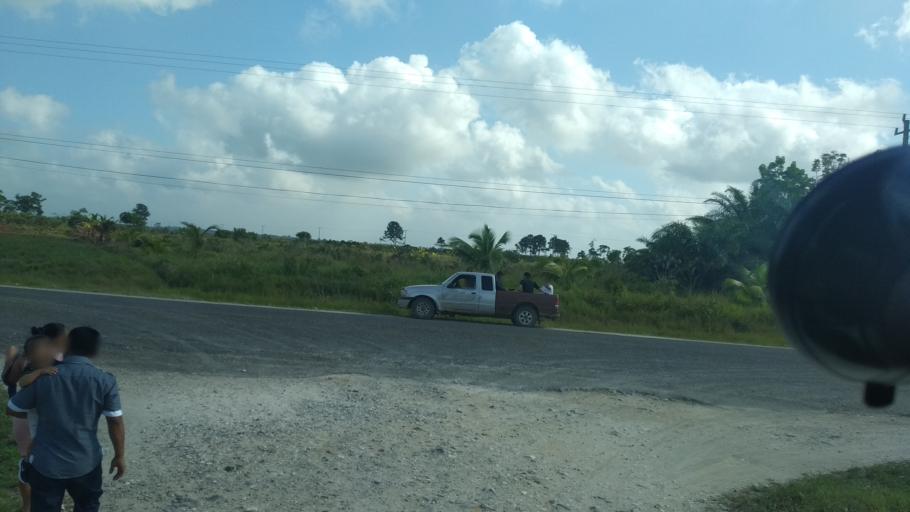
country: BZ
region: Stann Creek
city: Placencia
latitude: 16.5127
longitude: -88.5434
